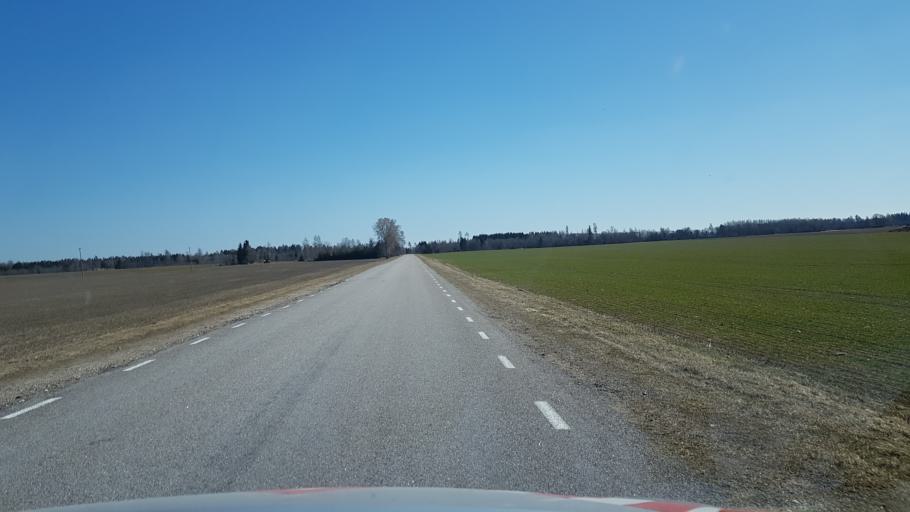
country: EE
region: Laeaene-Virumaa
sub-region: Vaeike-Maarja vald
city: Vaike-Maarja
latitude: 59.1037
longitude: 26.3894
